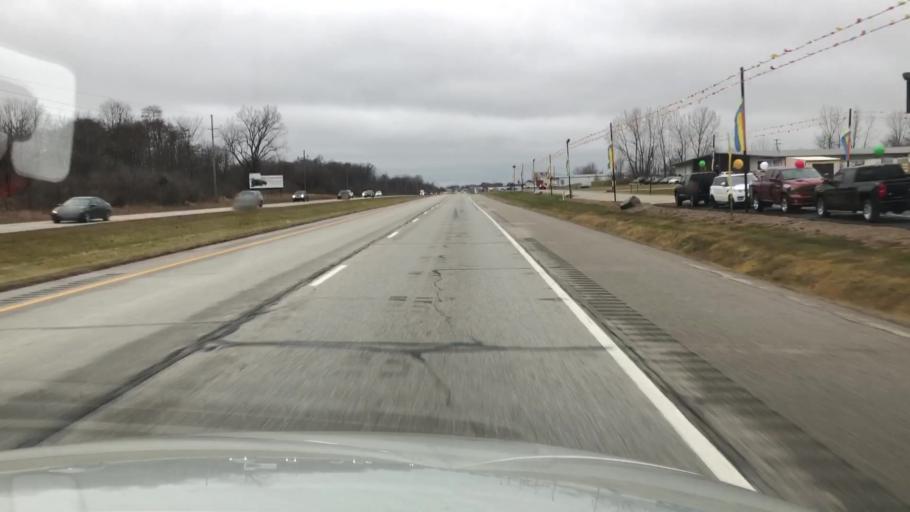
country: US
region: Indiana
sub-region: Kosciusko County
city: Winona Lake
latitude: 41.2177
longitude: -85.7669
